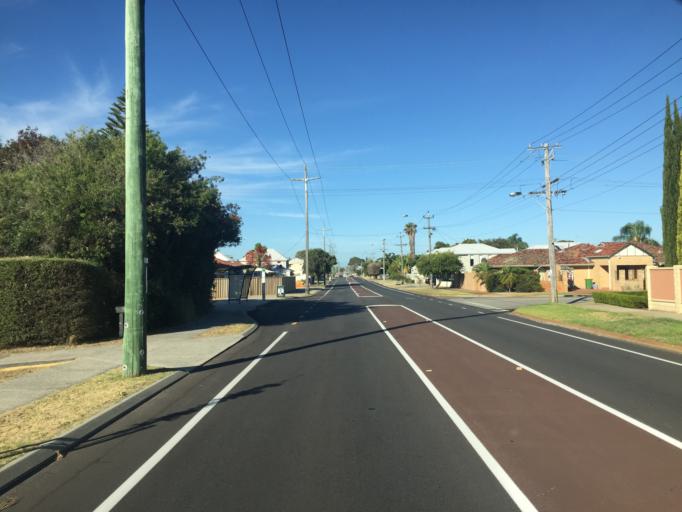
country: AU
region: Western Australia
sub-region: Belmont
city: Rivervale
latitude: -31.9643
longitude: 115.9245
